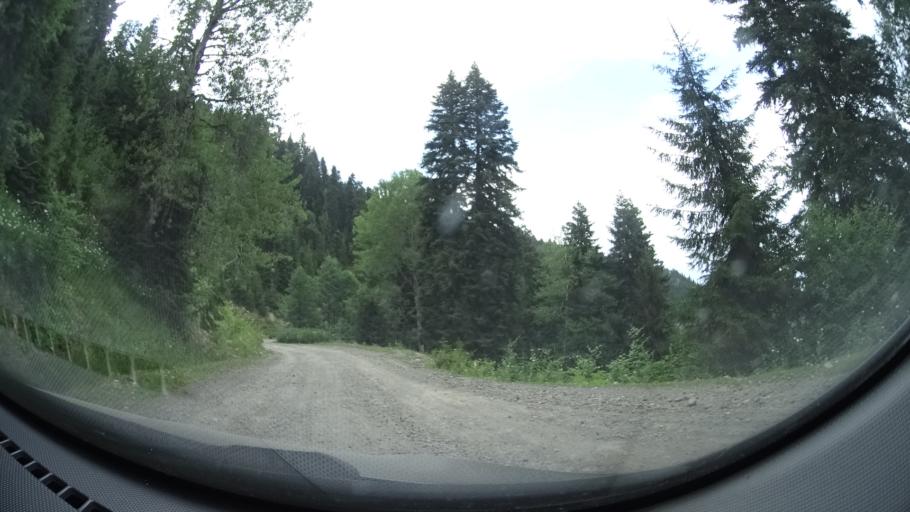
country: GE
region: Samtskhe-Javakheti
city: Adigeni
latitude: 41.6348
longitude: 42.5790
